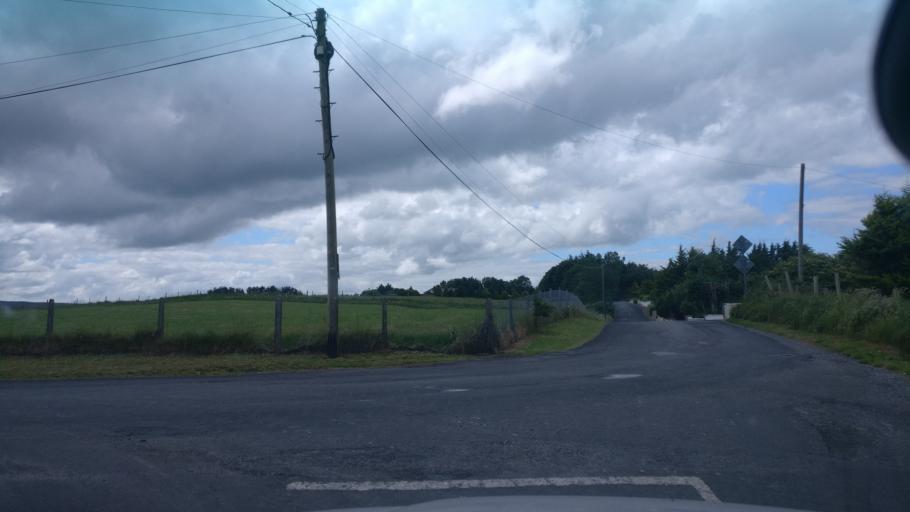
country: IE
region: Connaught
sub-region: County Galway
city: Loughrea
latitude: 53.1702
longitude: -8.5528
